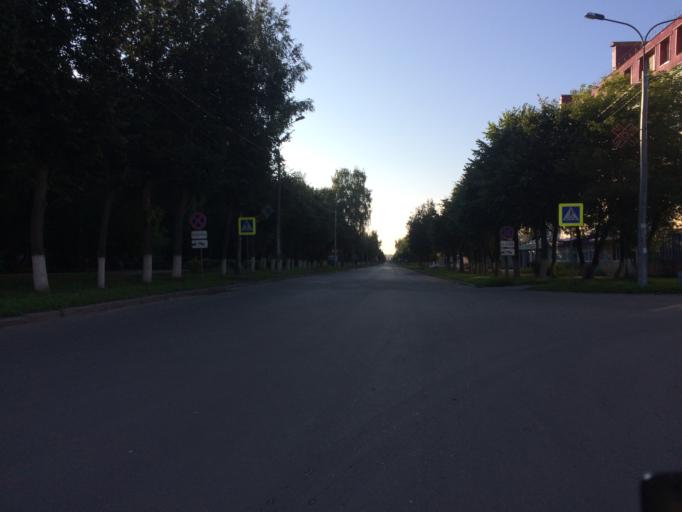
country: RU
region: Mariy-El
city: Yoshkar-Ola
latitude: 56.6416
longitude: 47.8786
